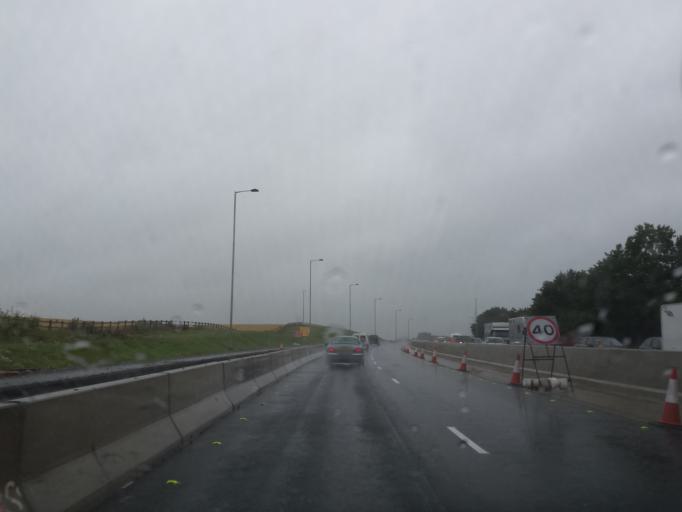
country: GB
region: England
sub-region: Coventry
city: Coventry
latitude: 52.3771
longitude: -1.4839
